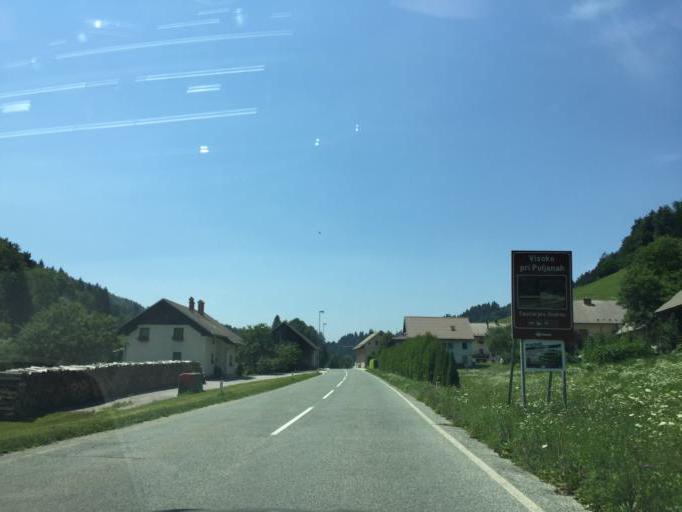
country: SI
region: Gorenja Vas-Poljane
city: Gorenja Vas
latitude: 46.1286
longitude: 14.2195
